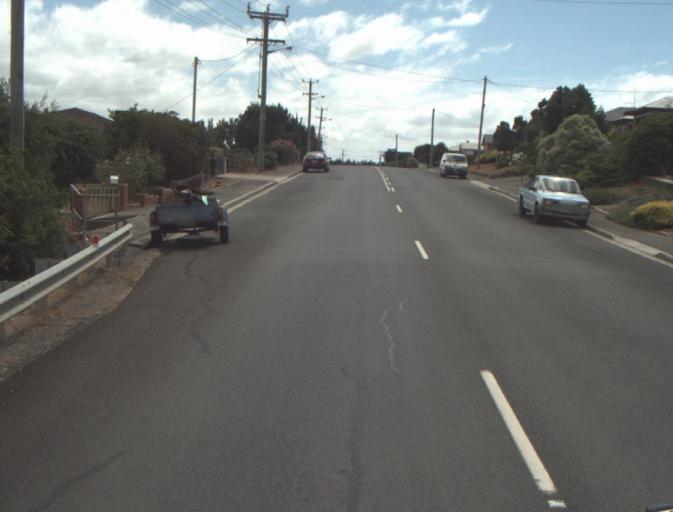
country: AU
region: Tasmania
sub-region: Launceston
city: Newstead
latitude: -41.4640
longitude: 147.2044
